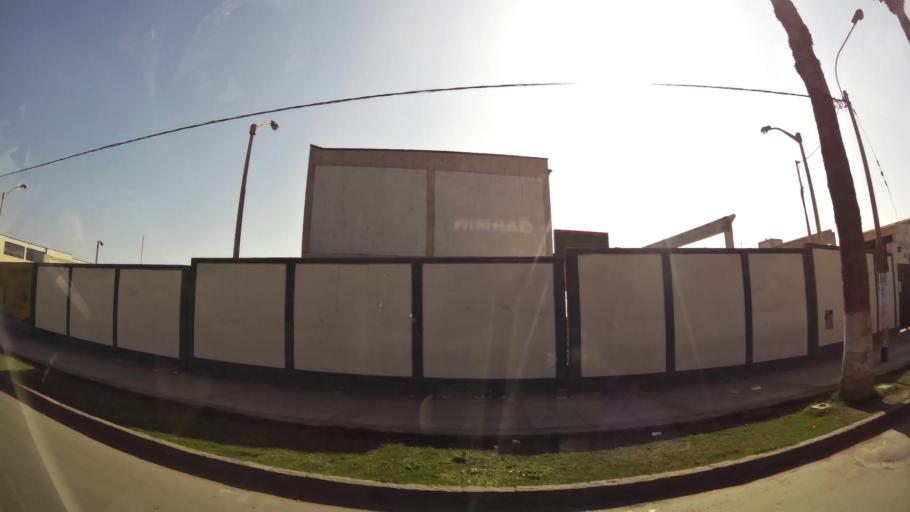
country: PE
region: Ica
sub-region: Provincia de Chincha
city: Chincha Alta
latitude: -13.4105
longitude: -76.1313
